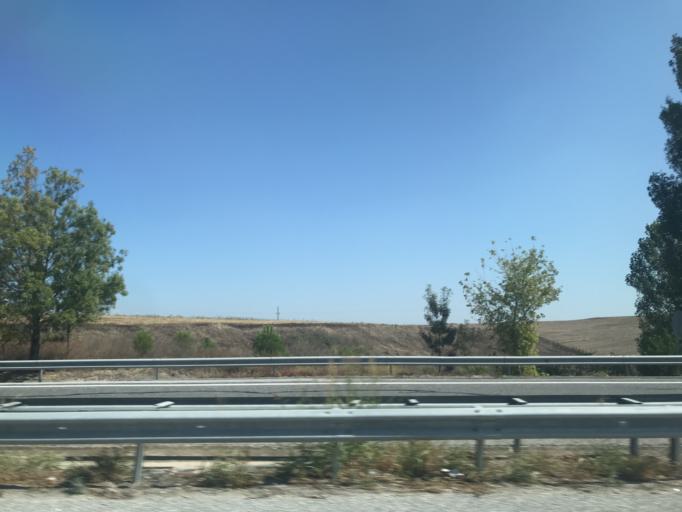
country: TR
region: Kirklareli
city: Luleburgaz
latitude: 41.4345
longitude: 27.3857
